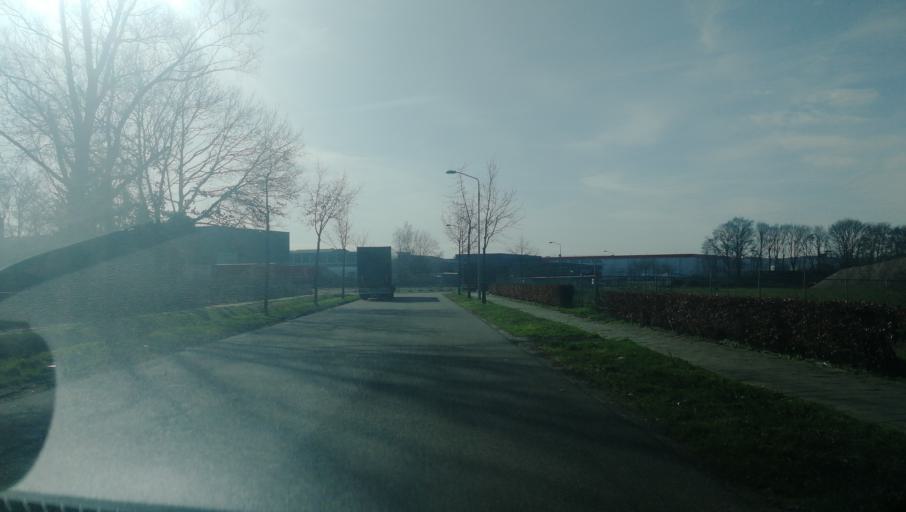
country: NL
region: Limburg
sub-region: Gemeente Venlo
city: Venlo
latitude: 51.3917
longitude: 6.1810
